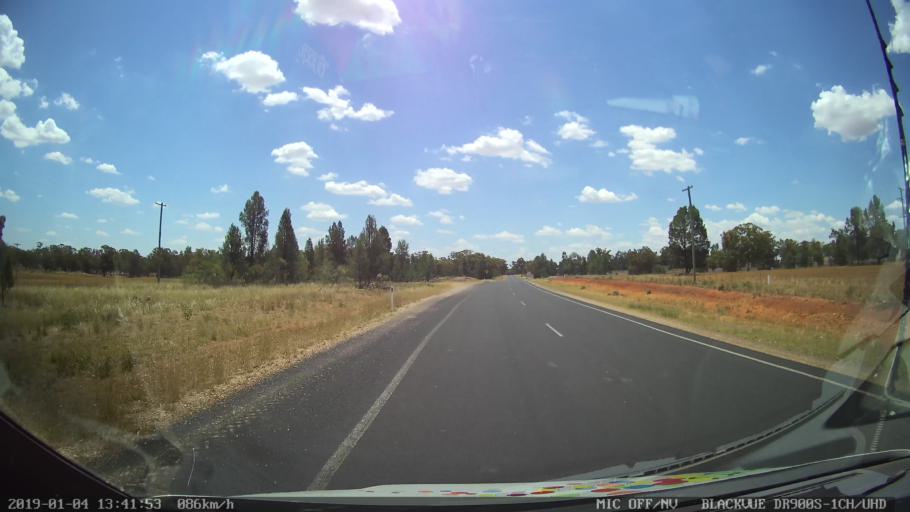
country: AU
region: New South Wales
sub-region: Dubbo Municipality
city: Dubbo
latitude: -32.4965
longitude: 148.5535
